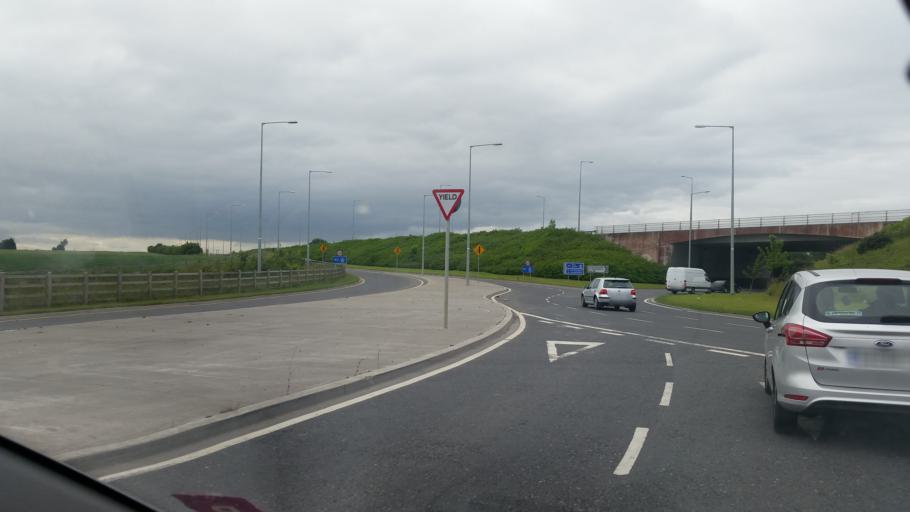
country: IE
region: Leinster
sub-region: Fingal County
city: Blanchardstown
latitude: 53.4322
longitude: -6.3469
